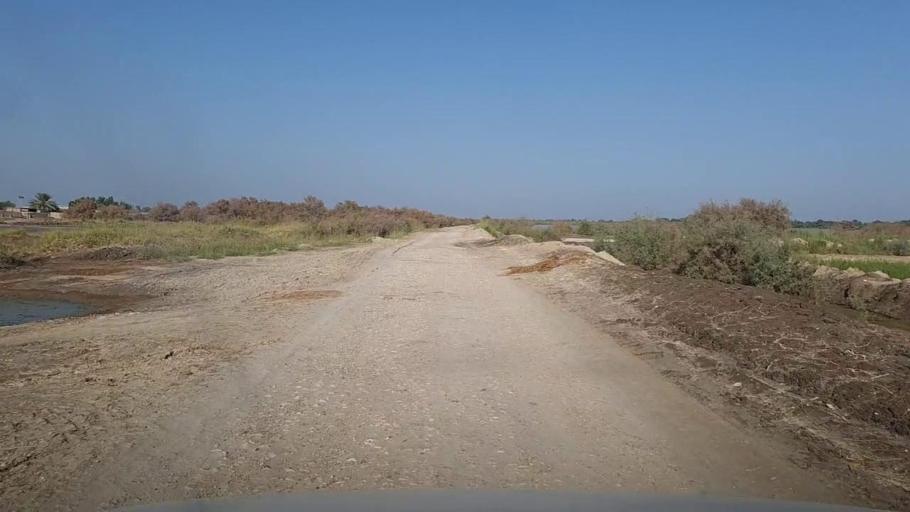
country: PK
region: Sindh
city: Kandhkot
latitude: 28.2803
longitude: 69.3244
